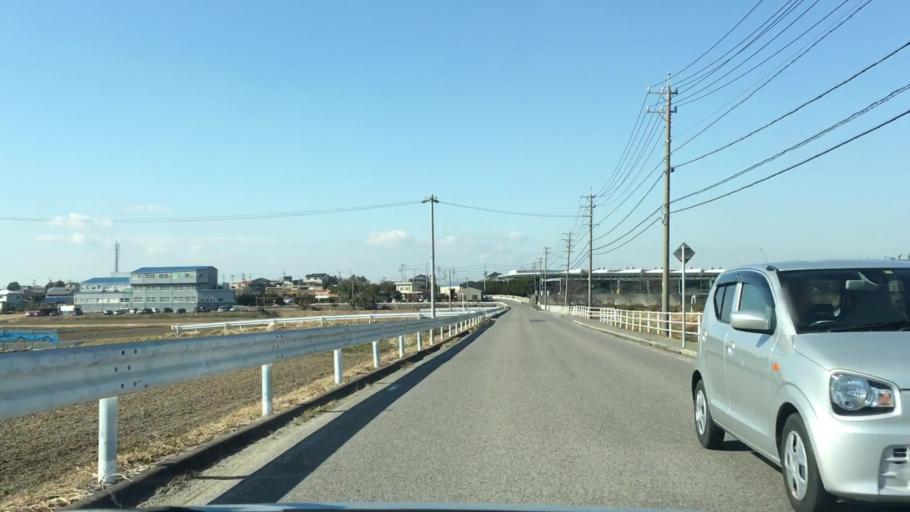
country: JP
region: Aichi
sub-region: Toyota-shi
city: Toyota
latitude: 35.0320
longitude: 137.1294
